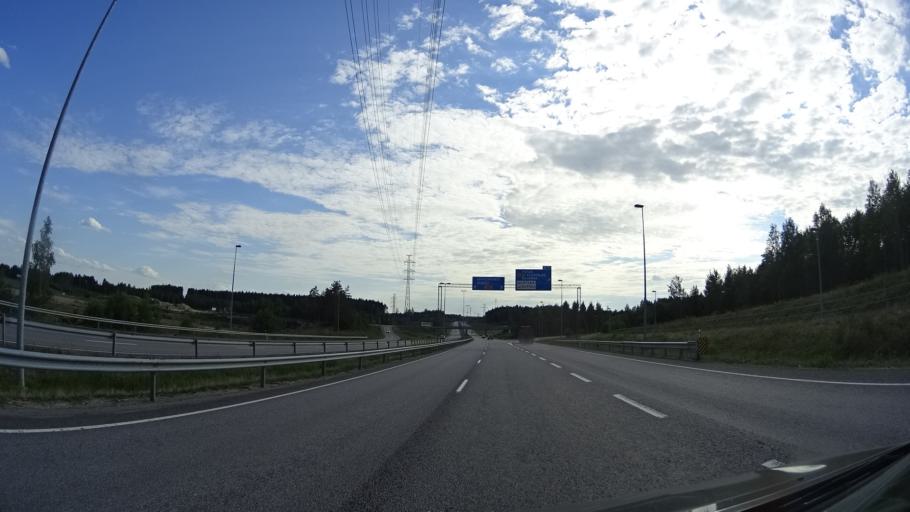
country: FI
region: South Karelia
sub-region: Lappeenranta
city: Lappeenranta
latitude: 61.0685
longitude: 28.2987
